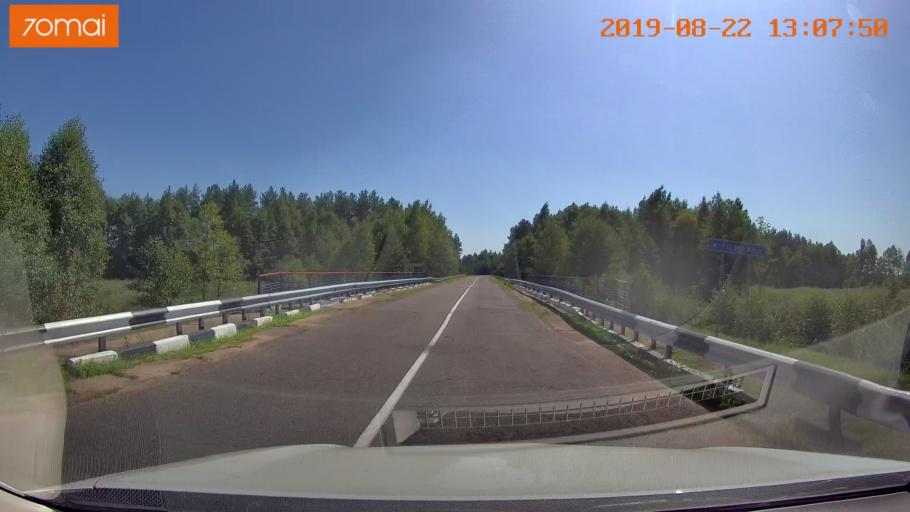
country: BY
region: Minsk
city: Prawdzinski
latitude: 53.3315
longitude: 27.8396
